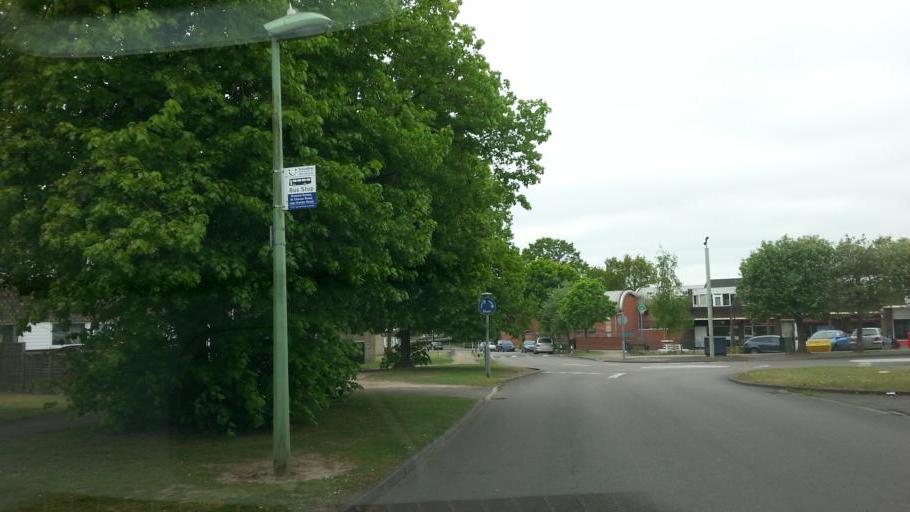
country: GB
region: England
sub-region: Suffolk
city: Bury St Edmunds
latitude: 52.2594
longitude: 0.6962
